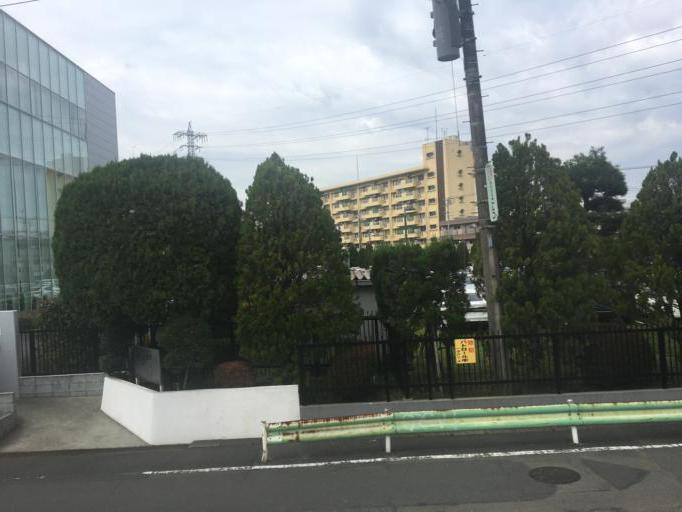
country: JP
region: Tokyo
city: Hino
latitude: 35.6685
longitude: 139.3628
